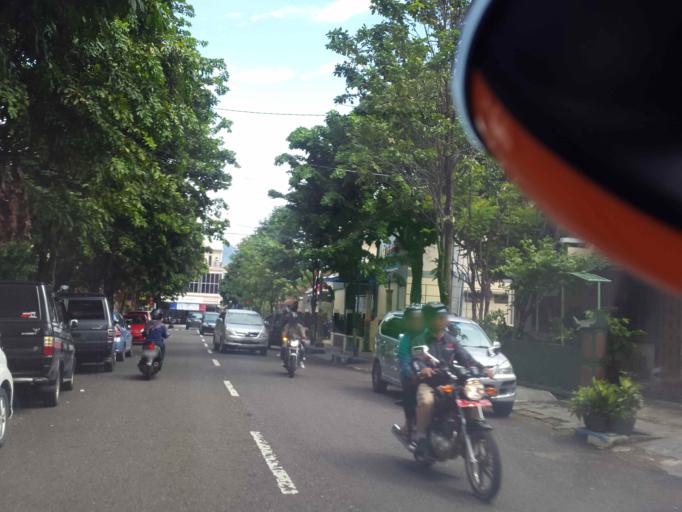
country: ID
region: Central Java
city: Wonosobo
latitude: -7.3937
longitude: 109.6959
